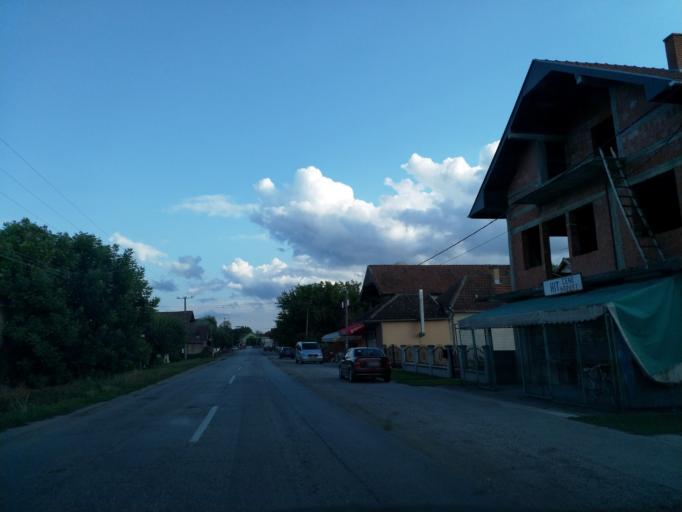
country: RS
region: Central Serbia
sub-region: Rasinski Okrug
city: Cicevac
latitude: 43.7662
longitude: 21.4287
